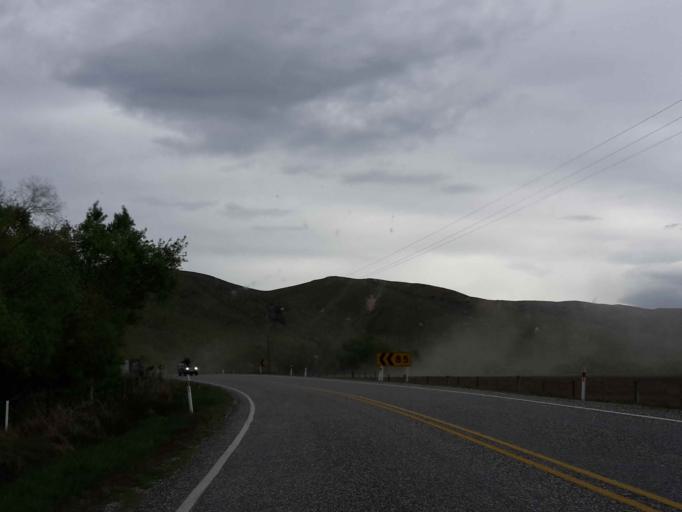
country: NZ
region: Otago
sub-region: Queenstown-Lakes District
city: Wanaka
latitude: -44.7053
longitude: 169.5028
